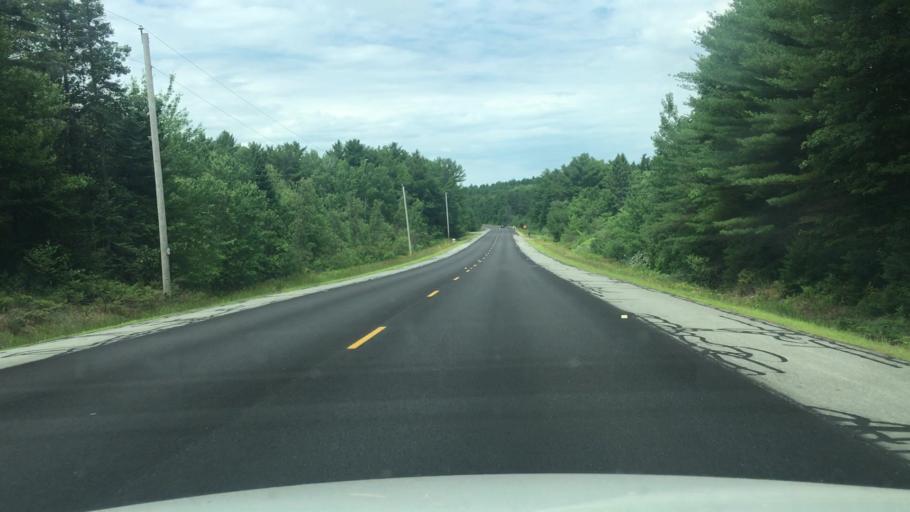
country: US
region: Maine
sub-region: Waldo County
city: Palermo
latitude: 44.4035
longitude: -69.4783
